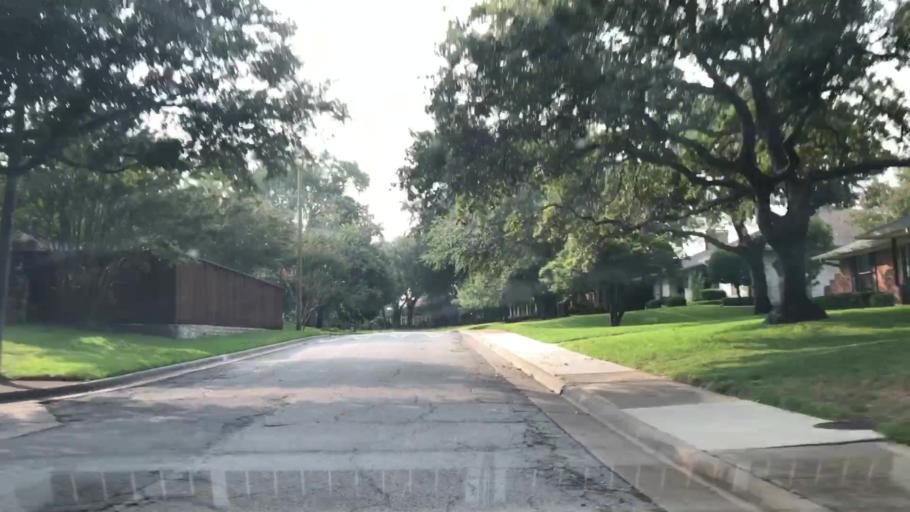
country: US
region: Texas
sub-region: Dallas County
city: Richardson
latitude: 32.9041
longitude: -96.7293
